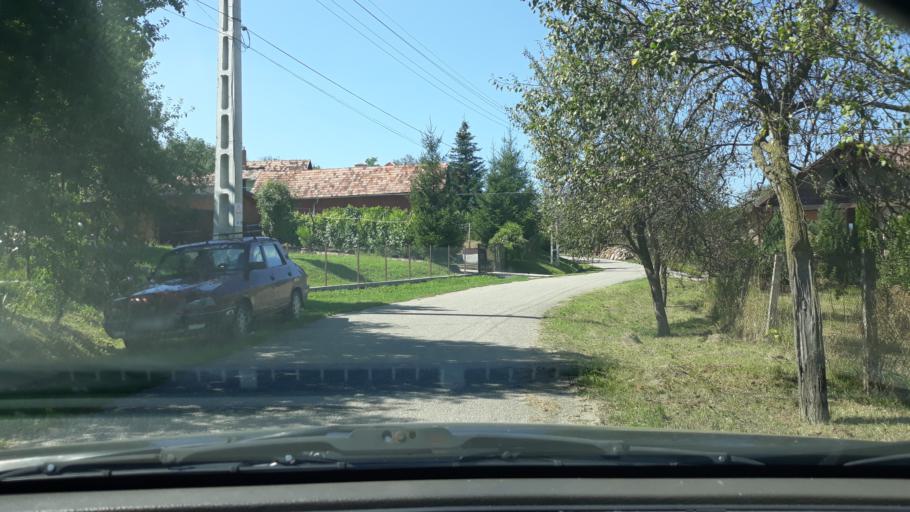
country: RO
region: Salaj
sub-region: Comuna Dobrin
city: Dobrin
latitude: 47.2944
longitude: 23.0921
